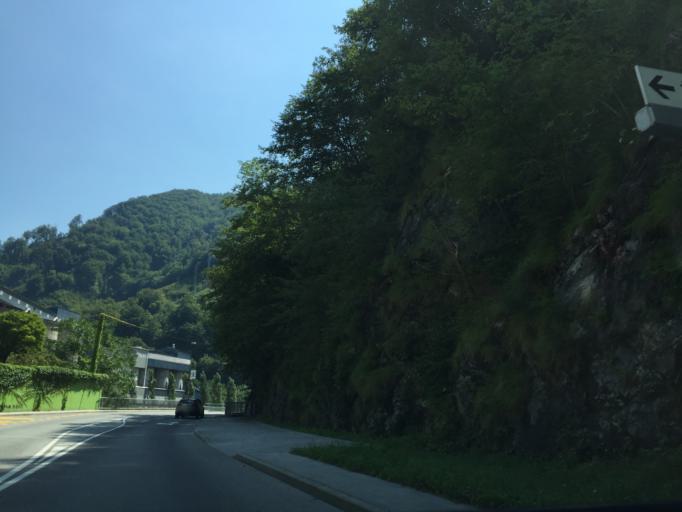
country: SI
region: Trbovlje
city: Trbovlje
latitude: 46.1276
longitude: 15.0348
